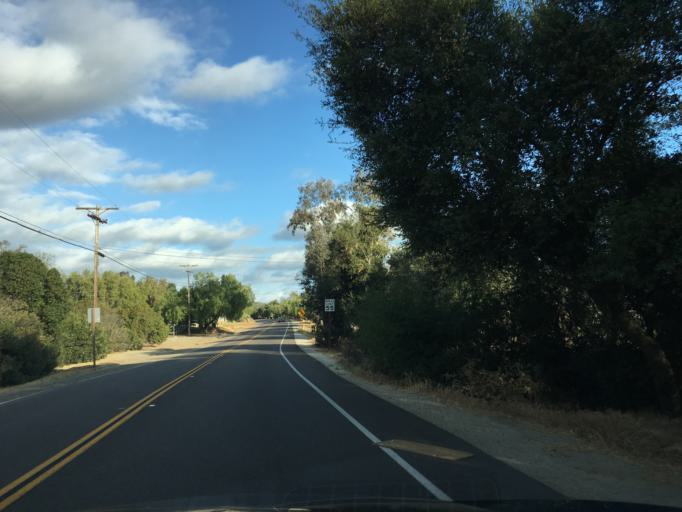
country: US
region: California
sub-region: San Diego County
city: Valley Center
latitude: 33.2355
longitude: -117.0506
